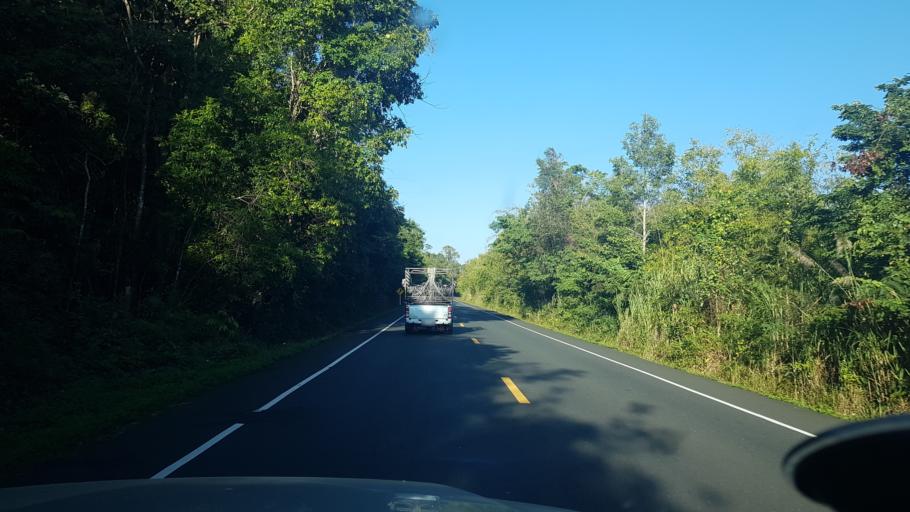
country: TH
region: Phetchabun
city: Nam Nao
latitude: 16.7023
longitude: 101.6116
